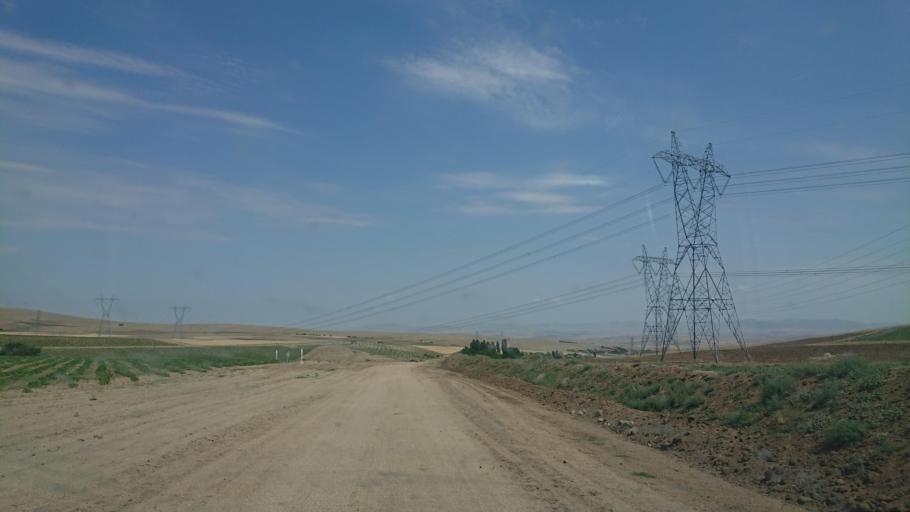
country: TR
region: Aksaray
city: Agacoren
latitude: 38.9006
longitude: 33.9244
